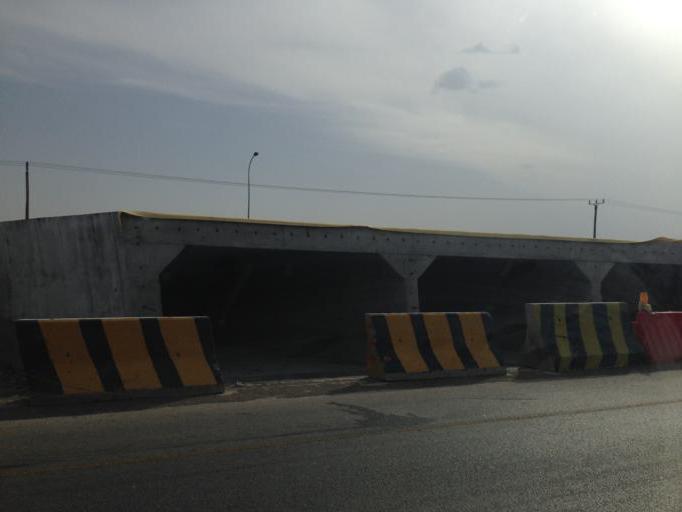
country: OM
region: Ash Sharqiyah
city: Al Qabil
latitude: 22.5650
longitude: 58.7051
